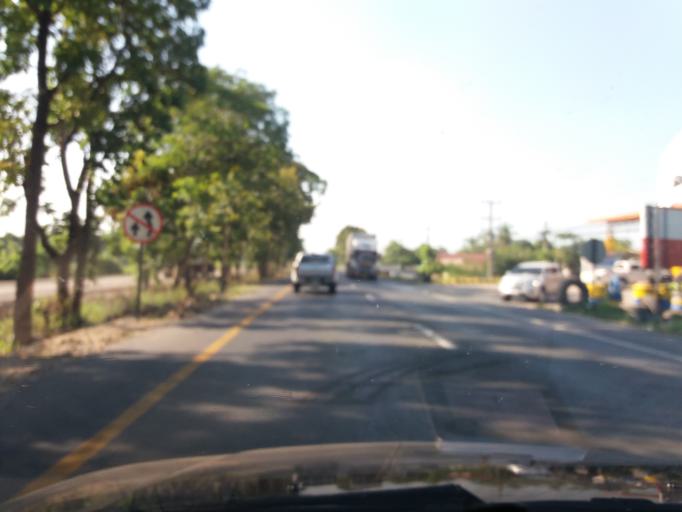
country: TH
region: Nakhon Sawan
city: Kao Liao
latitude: 15.7483
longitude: 100.0062
